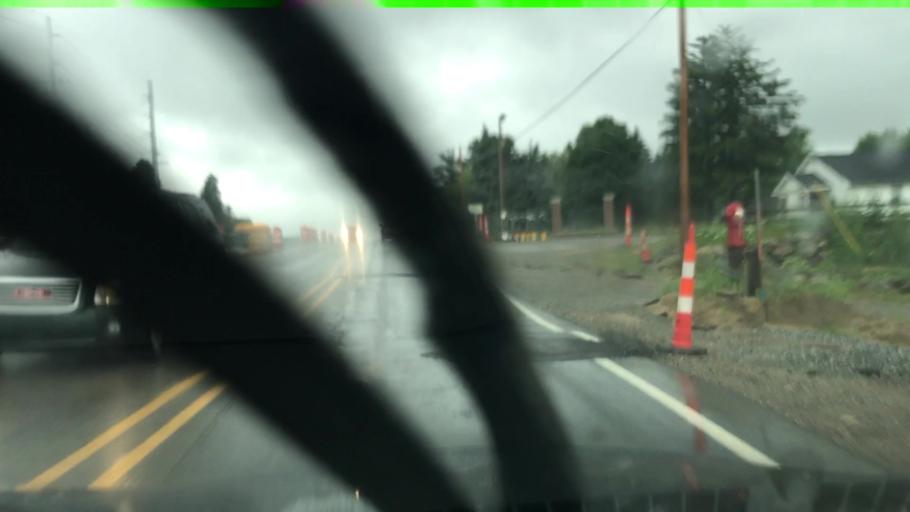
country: US
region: Michigan
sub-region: Oakland County
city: Auburn Hills
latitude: 42.7181
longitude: -83.3073
